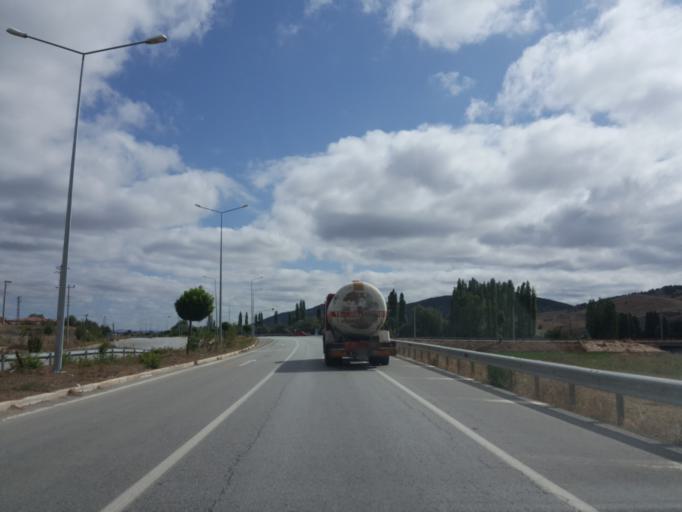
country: TR
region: Sivas
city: Yavu
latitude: 39.7971
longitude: 36.2001
